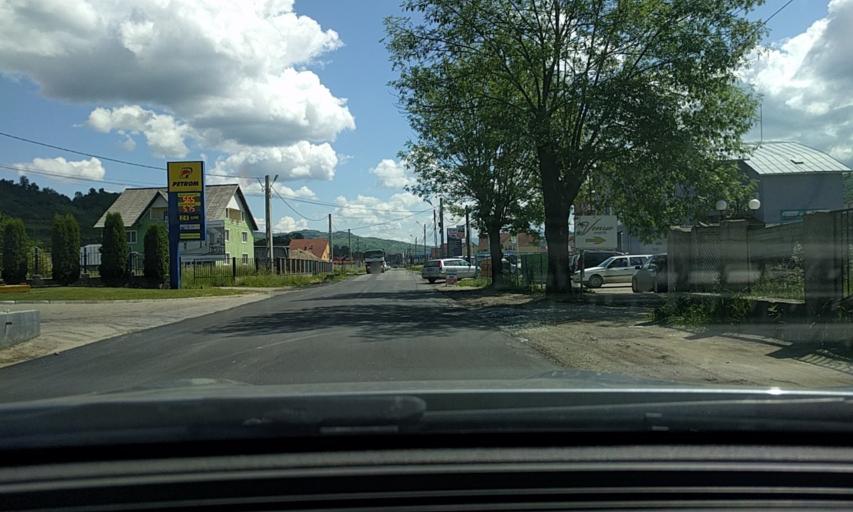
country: RO
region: Bistrita-Nasaud
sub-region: Oras Nasaud
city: Nasaud
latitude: 47.2845
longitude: 24.4230
